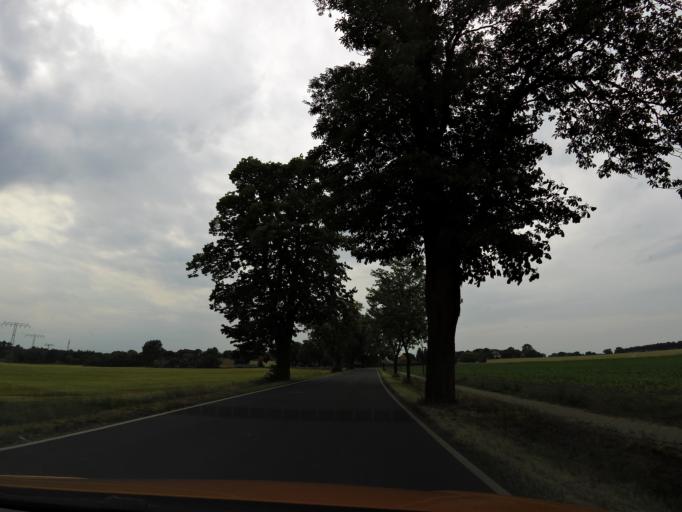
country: DE
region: Brandenburg
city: Zossen
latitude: 52.2240
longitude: 13.4196
